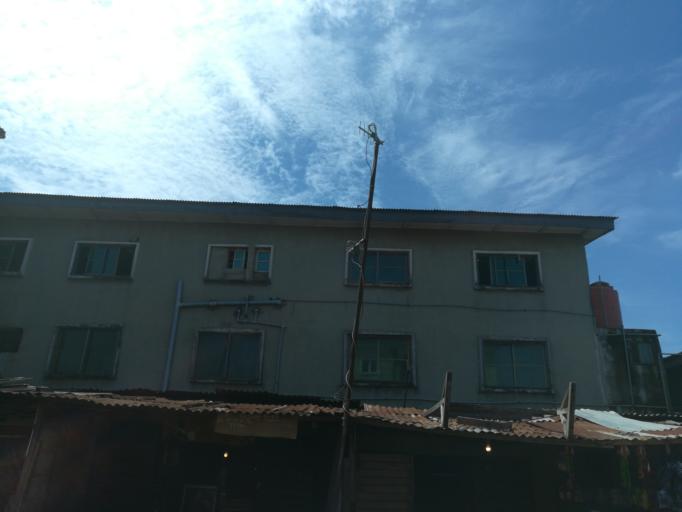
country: NG
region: Lagos
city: Oshodi
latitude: 6.5622
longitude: 3.3334
